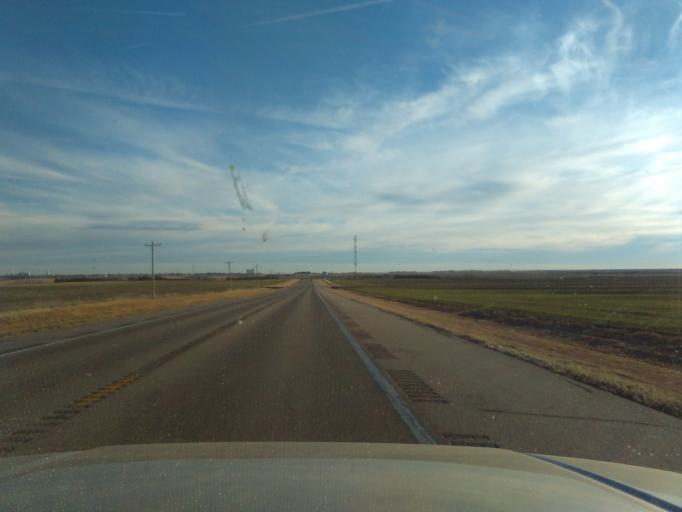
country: US
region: Kansas
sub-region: Logan County
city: Oakley
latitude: 39.1649
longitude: -100.8704
